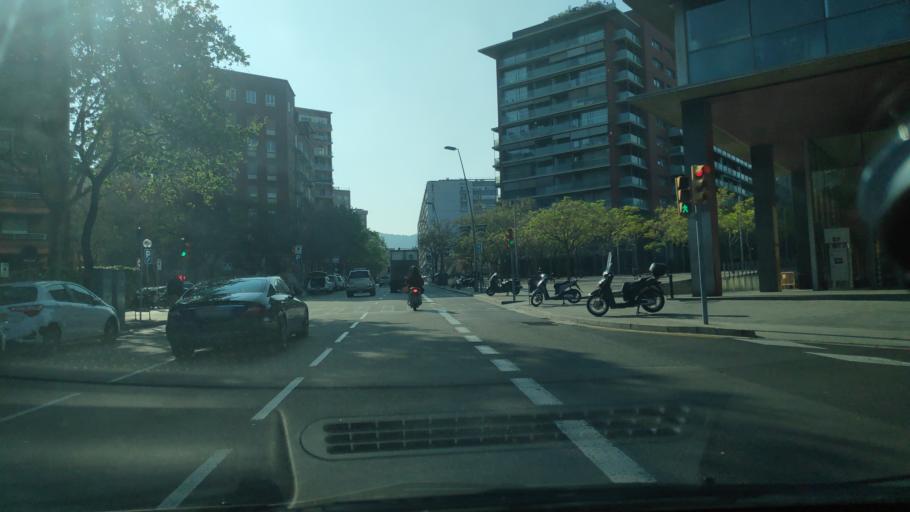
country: ES
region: Catalonia
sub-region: Provincia de Barcelona
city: les Corts
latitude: 41.3920
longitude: 2.1345
